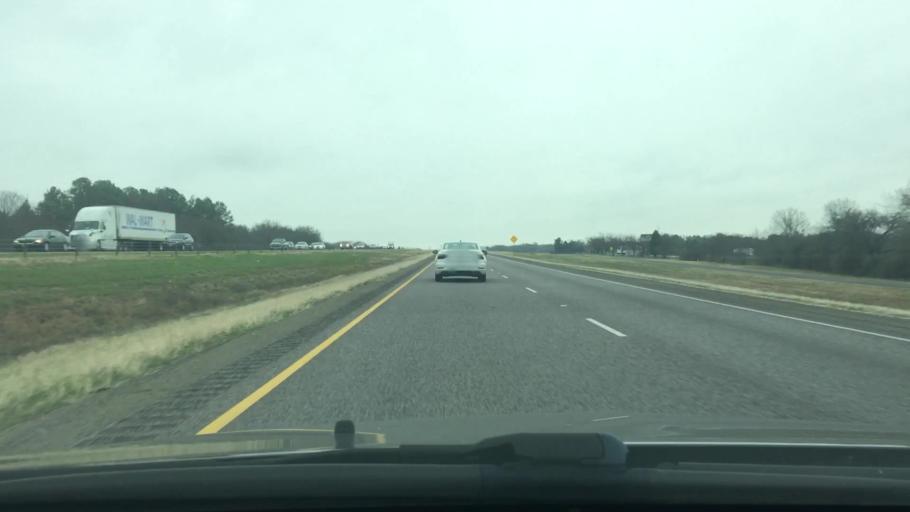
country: US
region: Texas
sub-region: Freestone County
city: Fairfield
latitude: 31.7760
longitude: -96.2270
